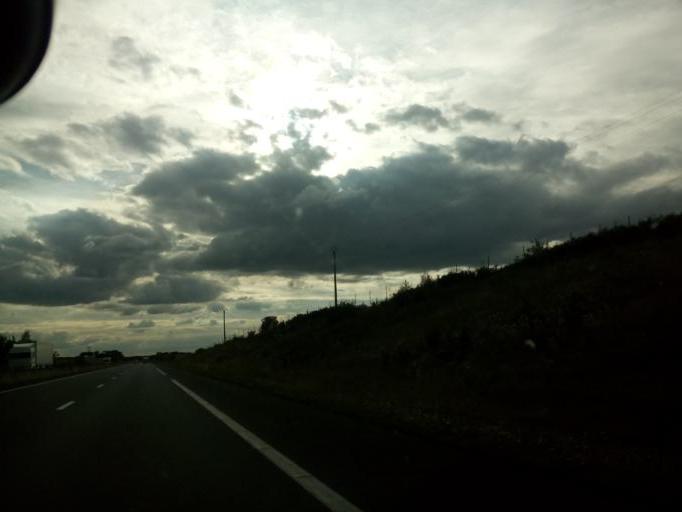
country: FR
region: Centre
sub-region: Departement du Loir-et-Cher
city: Saint-Georges-sur-Cher
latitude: 47.2918
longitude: 1.0960
